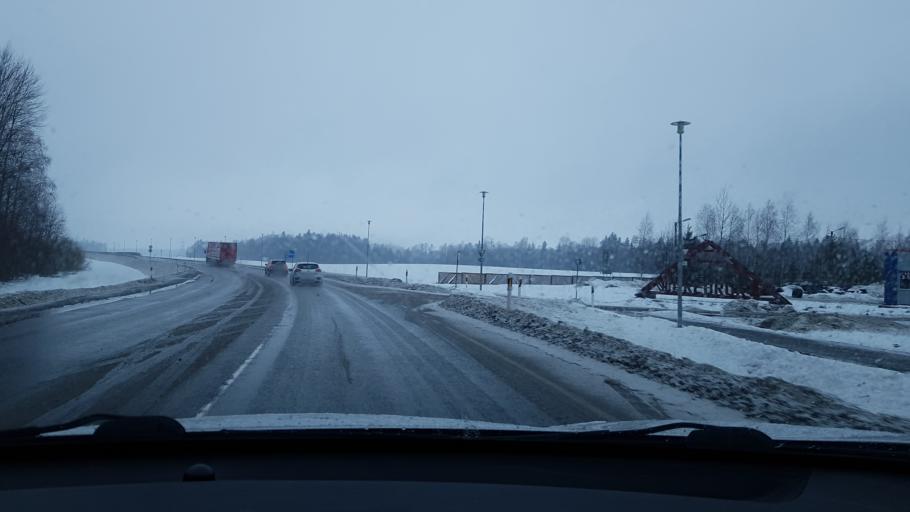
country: EE
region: Jaervamaa
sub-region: Paide linn
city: Paide
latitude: 58.8798
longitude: 25.5123
